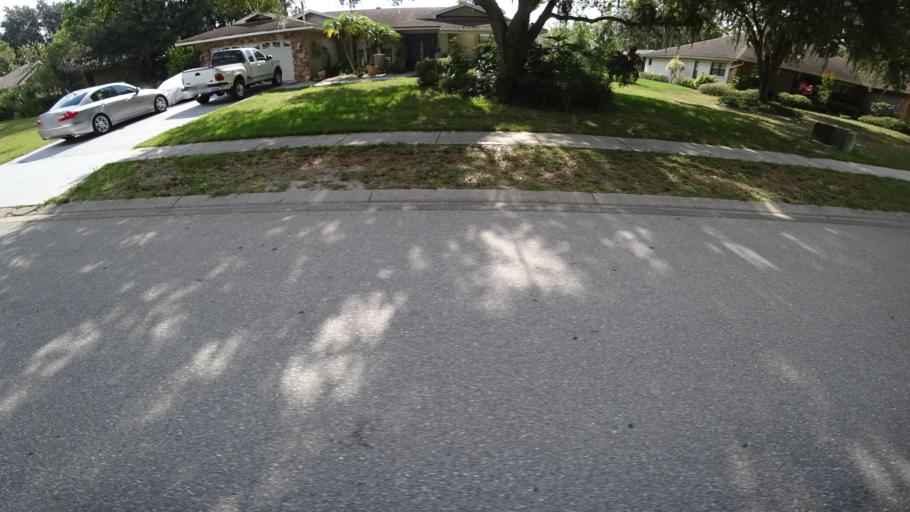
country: US
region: Florida
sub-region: Sarasota County
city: The Meadows
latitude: 27.4265
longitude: -82.4426
